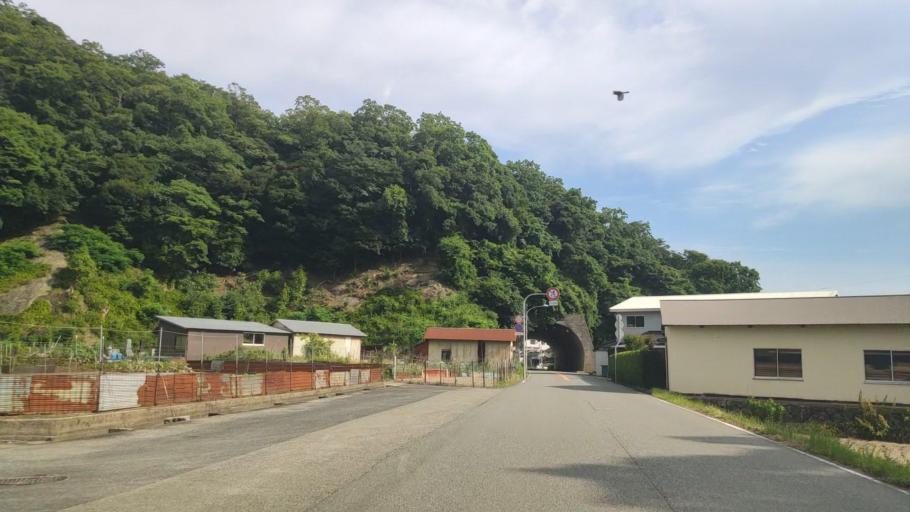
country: JP
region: Hyogo
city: Toyooka
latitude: 35.6388
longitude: 134.8361
